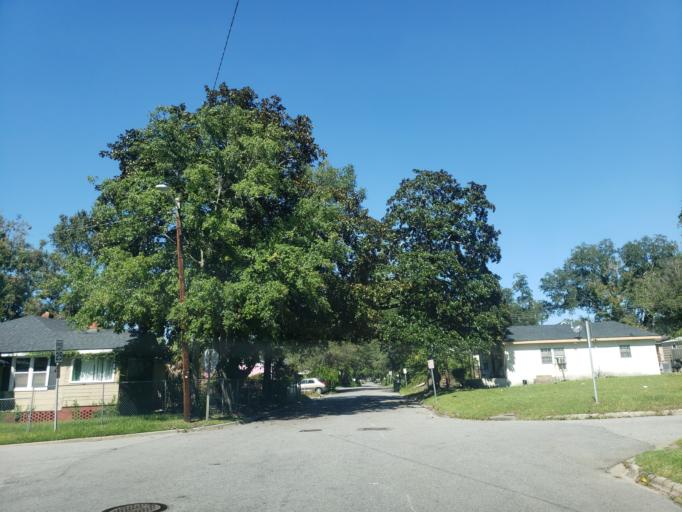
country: US
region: Georgia
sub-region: Chatham County
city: Savannah
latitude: 32.0516
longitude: -81.1115
